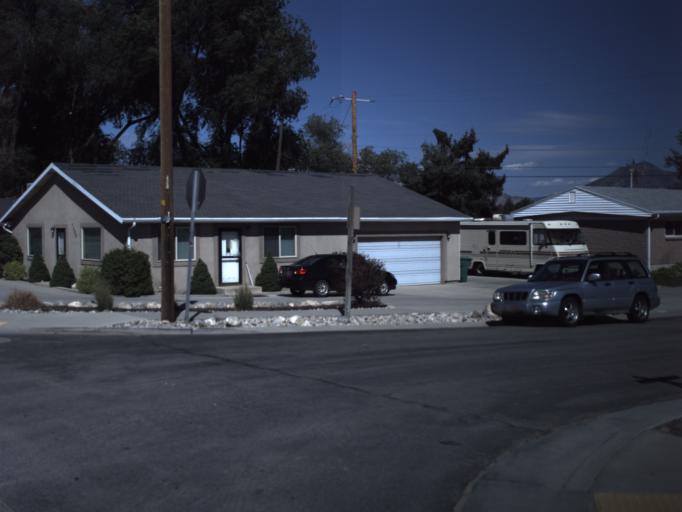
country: US
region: Utah
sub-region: Salt Lake County
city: West Jordan
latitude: 40.6145
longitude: -111.9386
